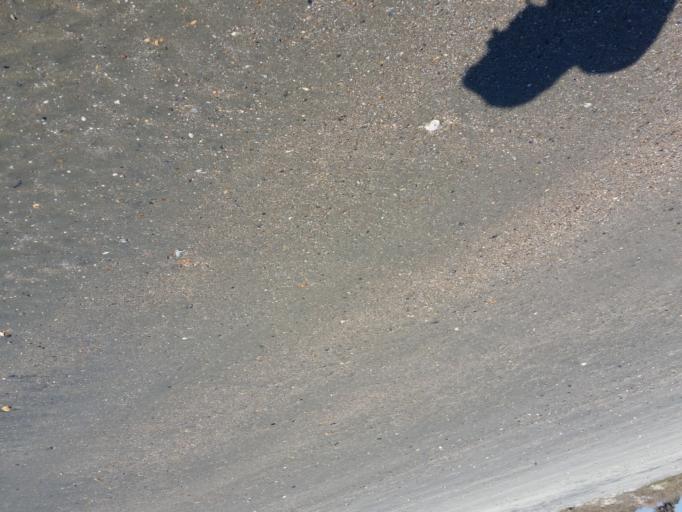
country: US
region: South Carolina
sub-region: Charleston County
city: Isle of Palms
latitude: 32.7974
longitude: -79.7526
